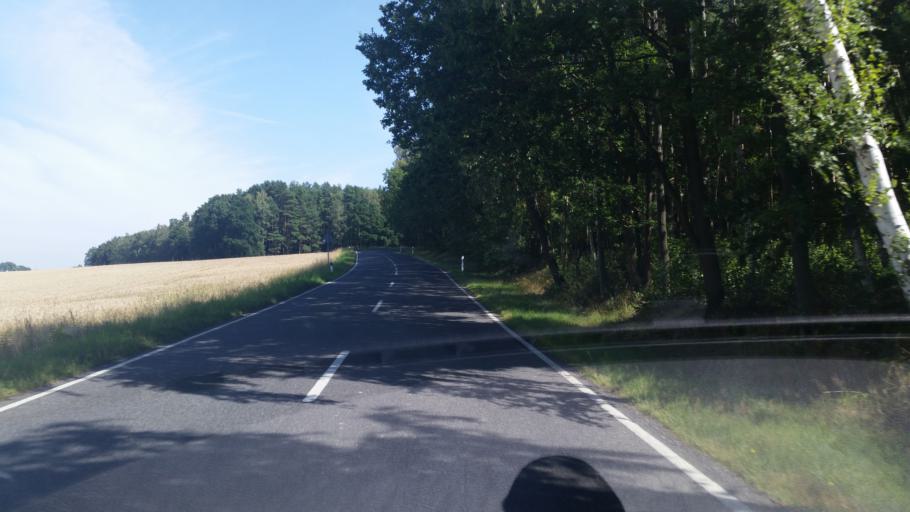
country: DE
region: Saxony
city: Neukirch
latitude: 51.3106
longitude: 14.0330
